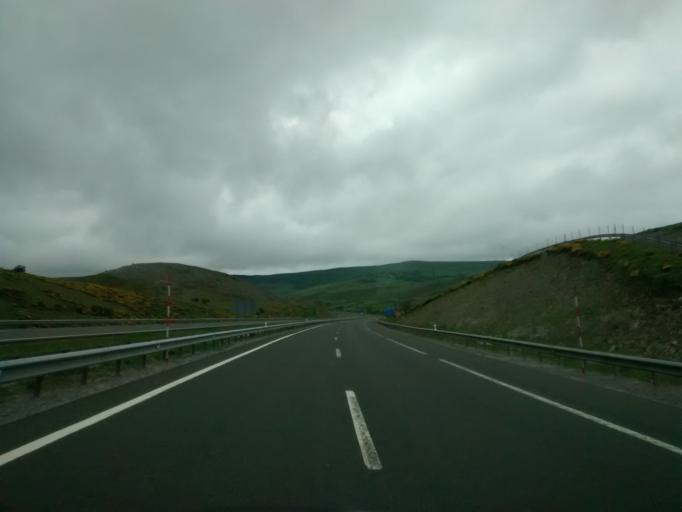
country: ES
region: Cantabria
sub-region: Provincia de Cantabria
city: Villaescusa
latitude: 42.9258
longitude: -4.1247
